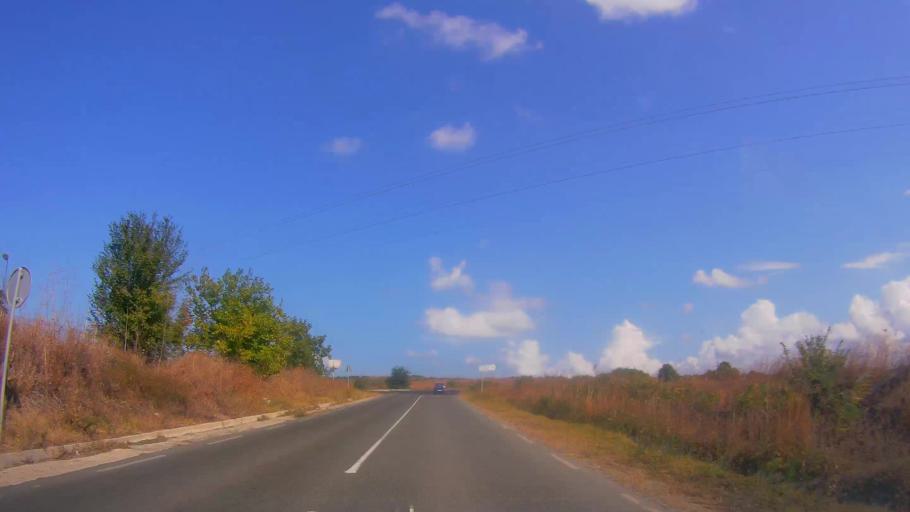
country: BG
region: Burgas
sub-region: Obshtina Burgas
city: Burgas
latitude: 42.4809
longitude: 27.3849
